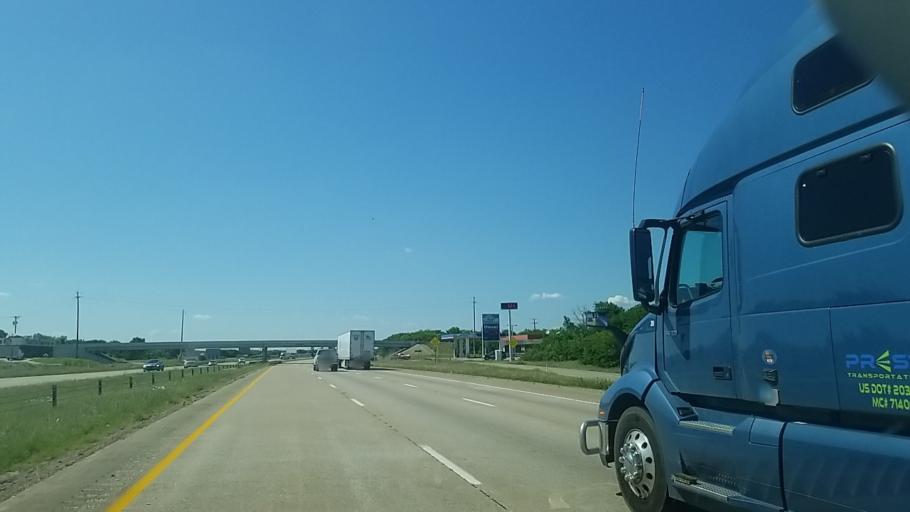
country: US
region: Texas
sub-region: Ellis County
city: Ennis
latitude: 32.3730
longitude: -96.6435
